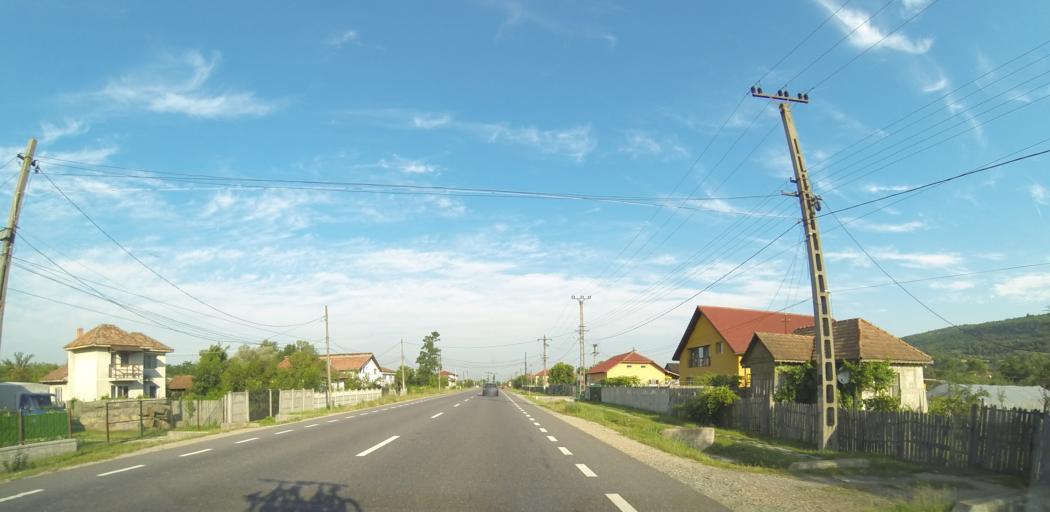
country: RO
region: Mehedinti
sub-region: Comuna Butoiesti
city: Butoiesti
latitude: 44.5847
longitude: 23.3578
